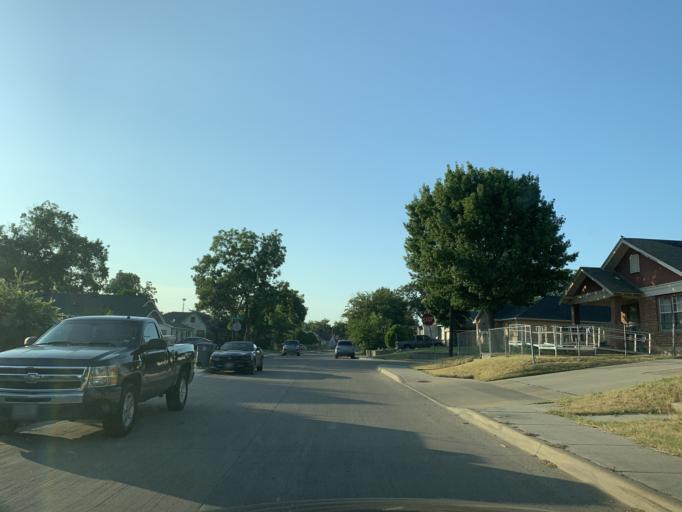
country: US
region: Texas
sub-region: Dallas County
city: Dallas
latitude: 32.7112
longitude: -96.8066
